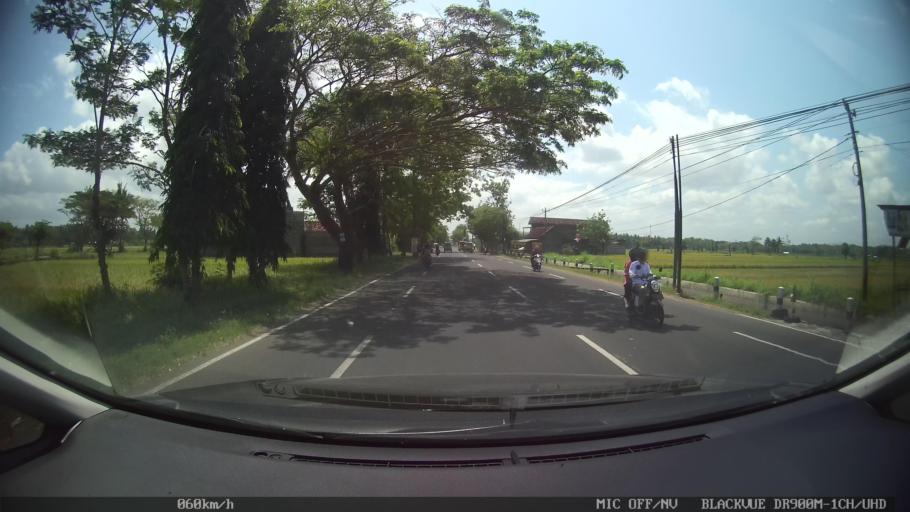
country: ID
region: Daerah Istimewa Yogyakarta
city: Pandak
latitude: -7.9236
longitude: 110.2802
